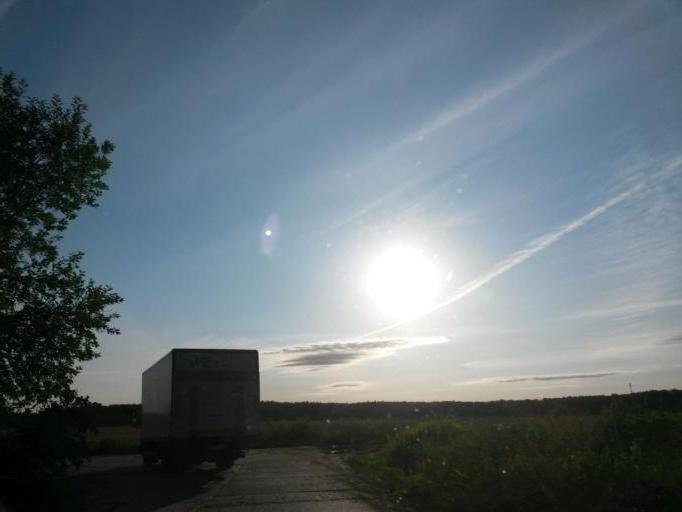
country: RU
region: Moskovskaya
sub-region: Podol'skiy Rayon
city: Podol'sk
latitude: 55.4027
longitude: 37.6287
